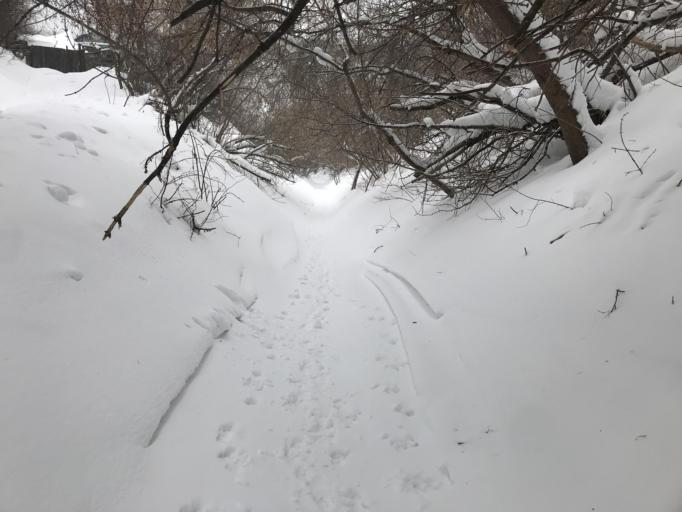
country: RU
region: Tjumen
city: Tobol'sk
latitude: 58.1996
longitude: 68.2586
